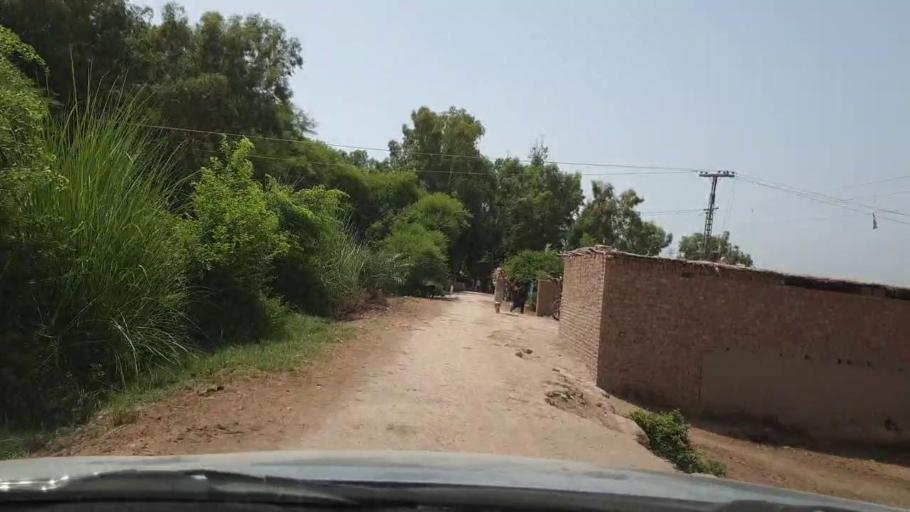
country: PK
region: Sindh
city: Pano Aqil
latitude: 27.9128
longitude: 69.1520
